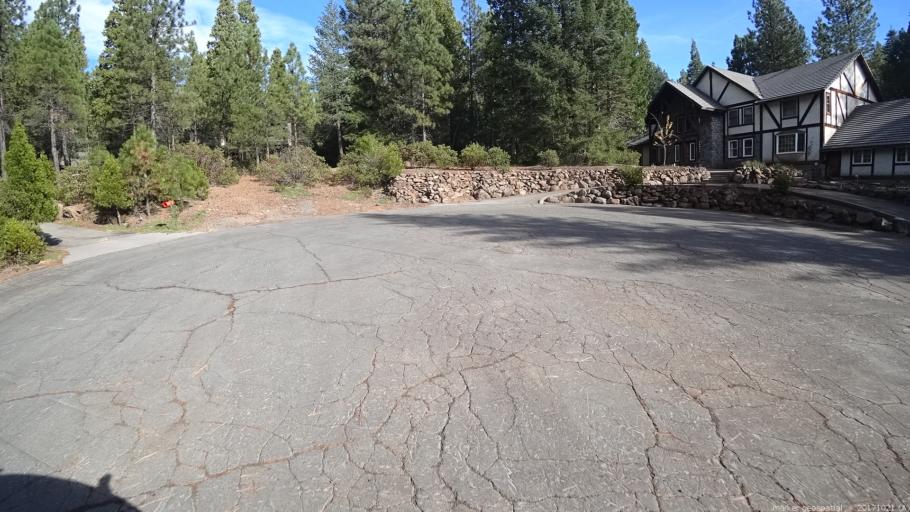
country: US
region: California
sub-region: Shasta County
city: Burney
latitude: 40.8707
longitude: -121.6638
